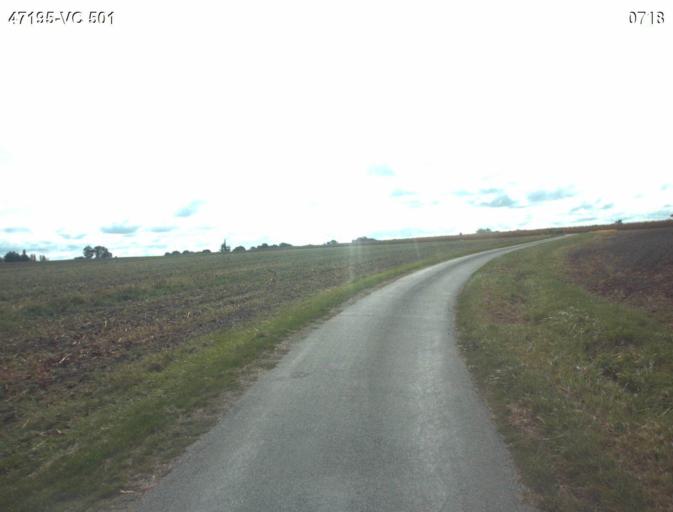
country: FR
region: Aquitaine
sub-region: Departement du Lot-et-Garonne
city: Nerac
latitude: 44.1022
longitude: 0.3179
